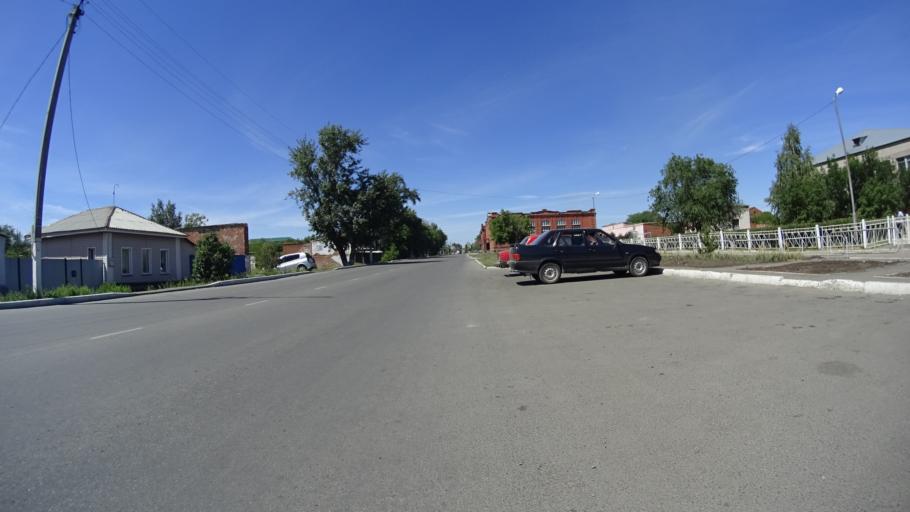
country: RU
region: Chelyabinsk
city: Troitsk
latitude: 54.0816
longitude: 61.5515
